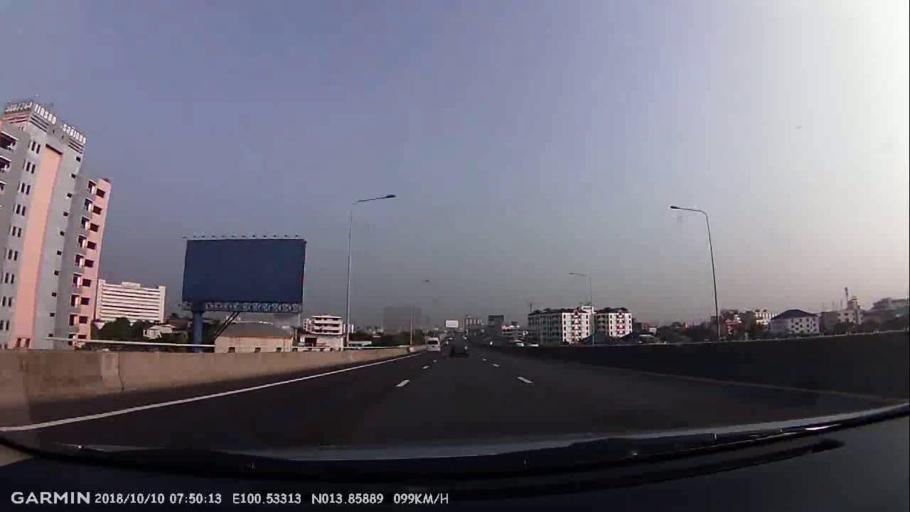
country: TH
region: Nonthaburi
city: Mueang Nonthaburi
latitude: 13.8591
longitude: 100.5331
